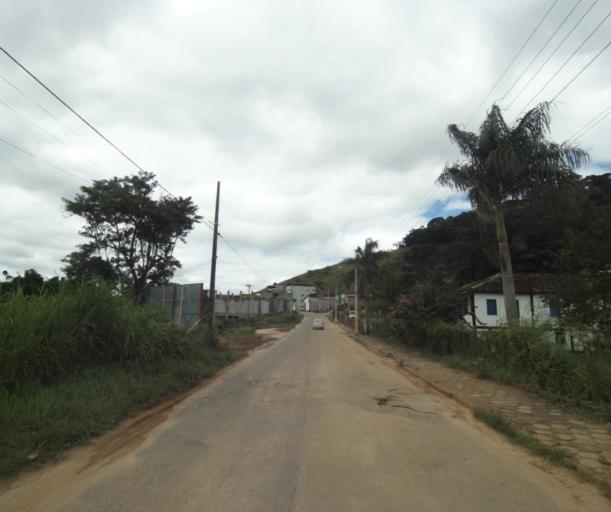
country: BR
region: Espirito Santo
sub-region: Irupi
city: Irupi
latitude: -20.3507
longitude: -41.6356
